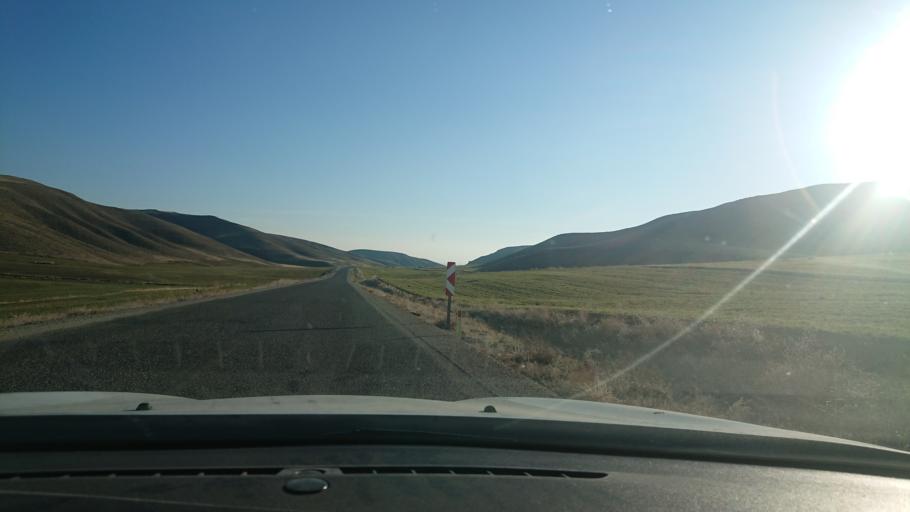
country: TR
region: Aksaray
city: Acipinar
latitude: 38.7066
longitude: 33.7566
